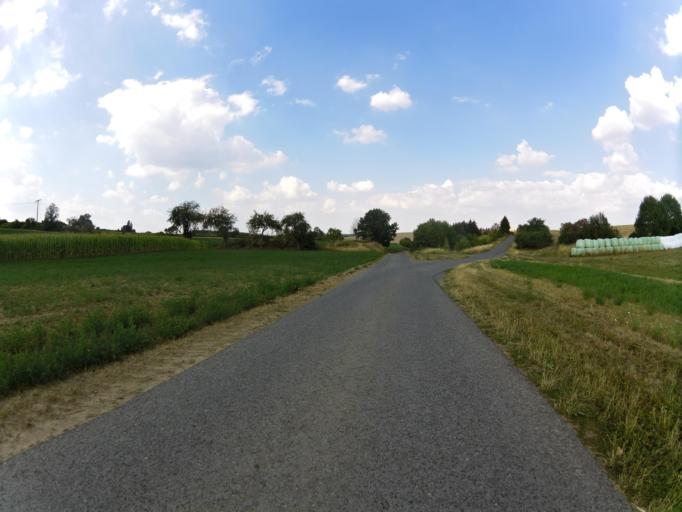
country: DE
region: Bavaria
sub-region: Regierungsbezirk Unterfranken
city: Ochsenfurt
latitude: 49.6476
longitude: 10.0601
